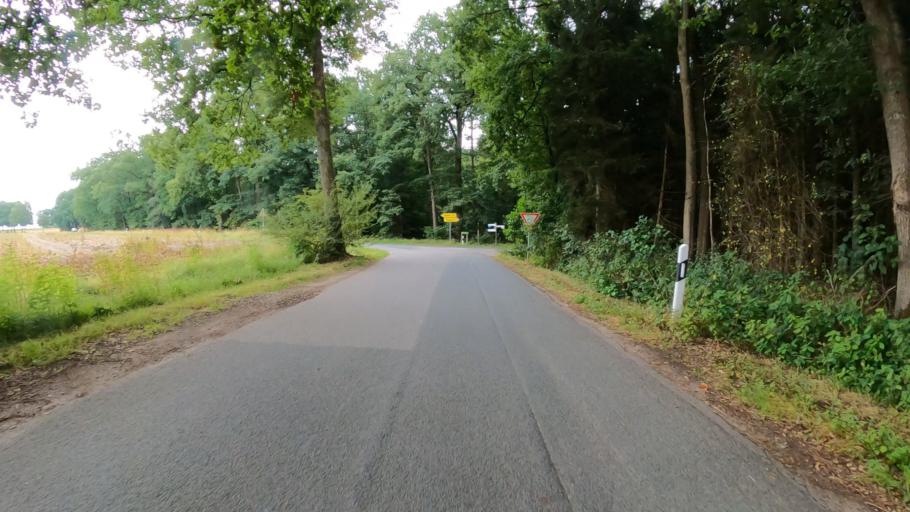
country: DE
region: Lower Saxony
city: Kakenstorf
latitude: 53.3242
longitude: 9.7532
